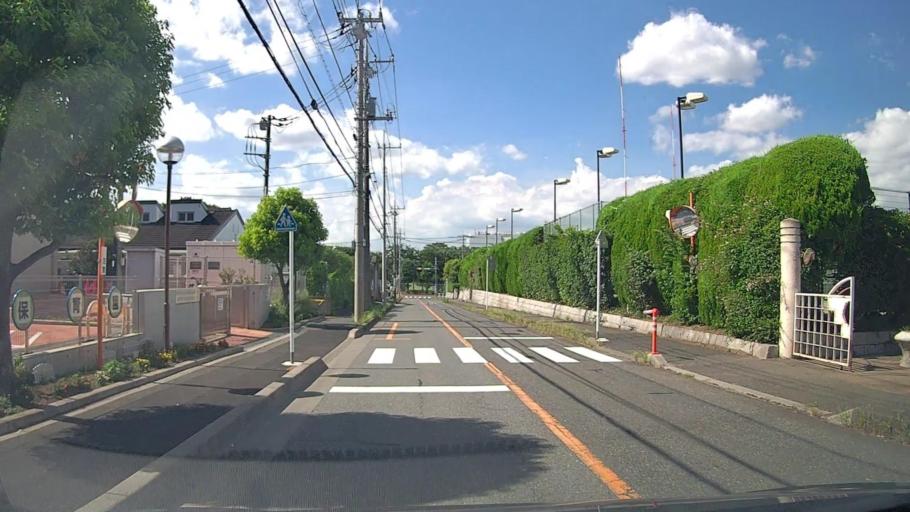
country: JP
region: Saitama
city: Wako
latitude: 35.7739
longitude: 139.6138
